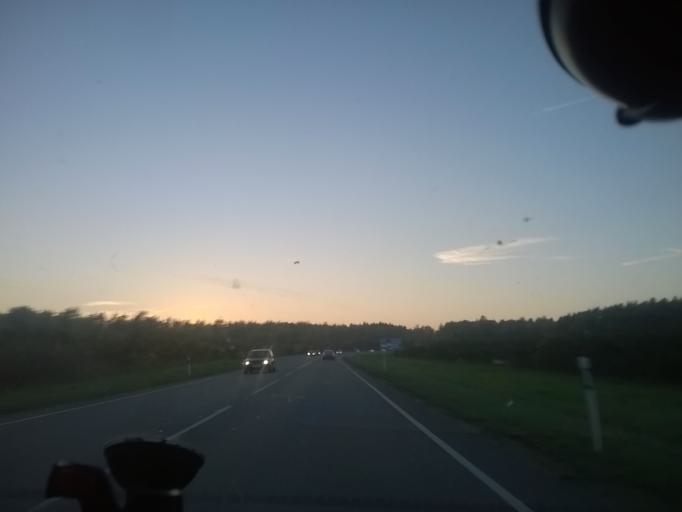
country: EE
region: Laeaene
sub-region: Ridala Parish
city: Uuemoisa
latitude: 58.9567
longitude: 23.7320
